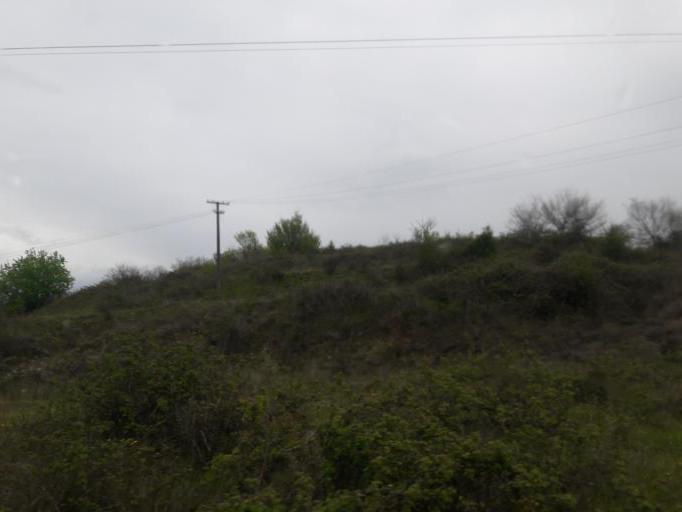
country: AL
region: Shkoder
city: Vukatane
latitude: 42.0130
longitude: 19.5351
